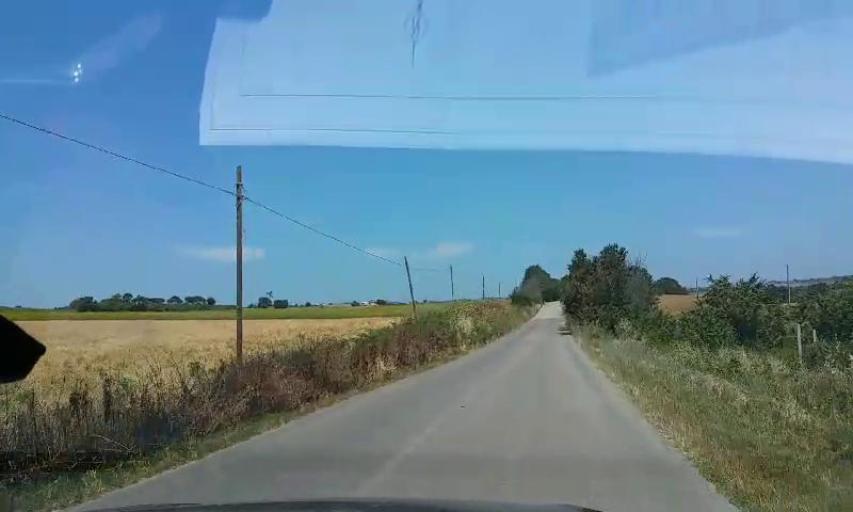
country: IT
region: Molise
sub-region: Provincia di Campobasso
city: Guglionesi
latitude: 41.9571
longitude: 14.9004
